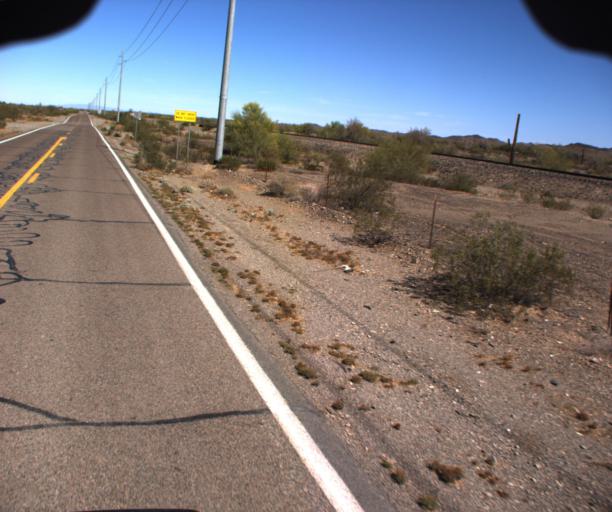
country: US
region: Arizona
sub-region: La Paz County
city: Salome
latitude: 33.7546
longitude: -113.7750
